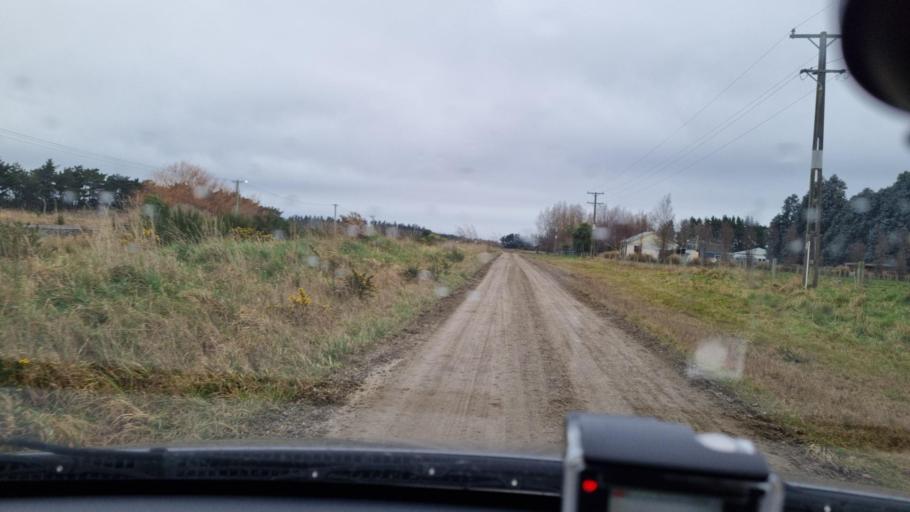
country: NZ
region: Southland
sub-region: Invercargill City
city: Invercargill
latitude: -46.3473
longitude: 168.3400
